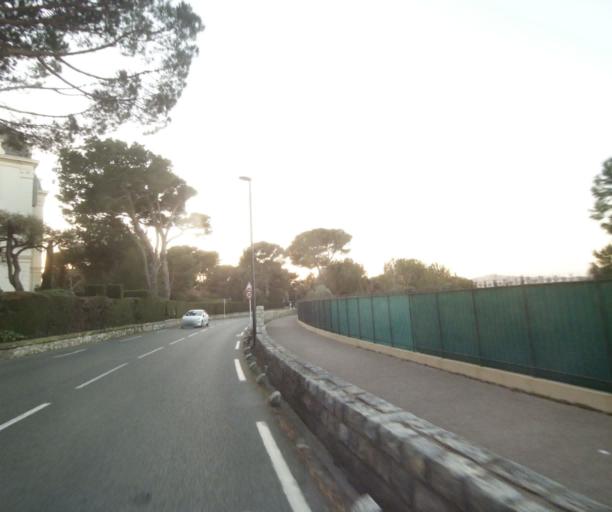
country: FR
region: Provence-Alpes-Cote d'Azur
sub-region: Departement des Alpes-Maritimes
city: Antibes
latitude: 43.5488
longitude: 7.1221
